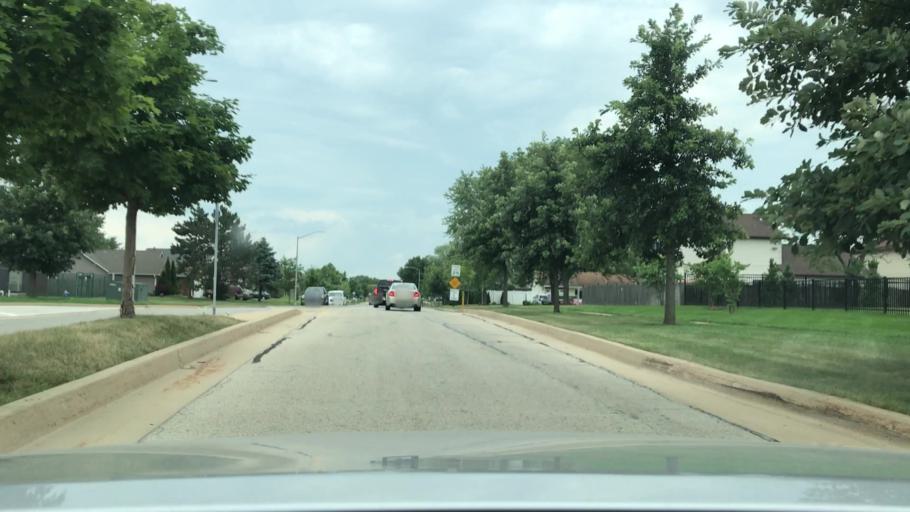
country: US
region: Illinois
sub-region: Will County
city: Bolingbrook
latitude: 41.7097
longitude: -88.0394
